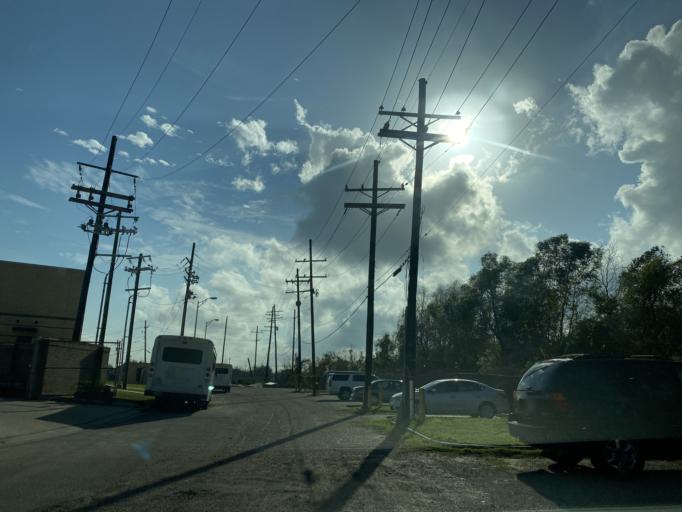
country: US
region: Louisiana
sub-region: Orleans Parish
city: New Orleans
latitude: 30.0261
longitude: -90.0464
